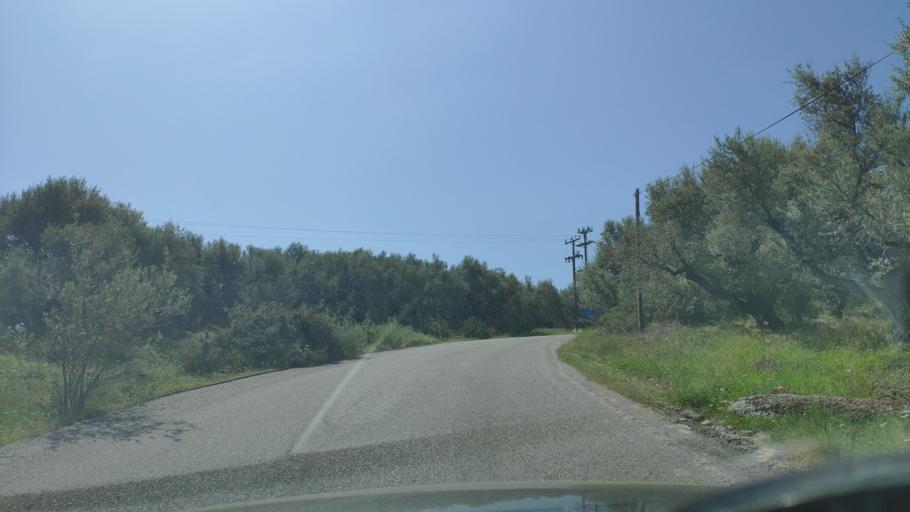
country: GR
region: West Greece
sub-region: Nomos Achaias
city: Aiyira
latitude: 38.1353
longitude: 22.3480
